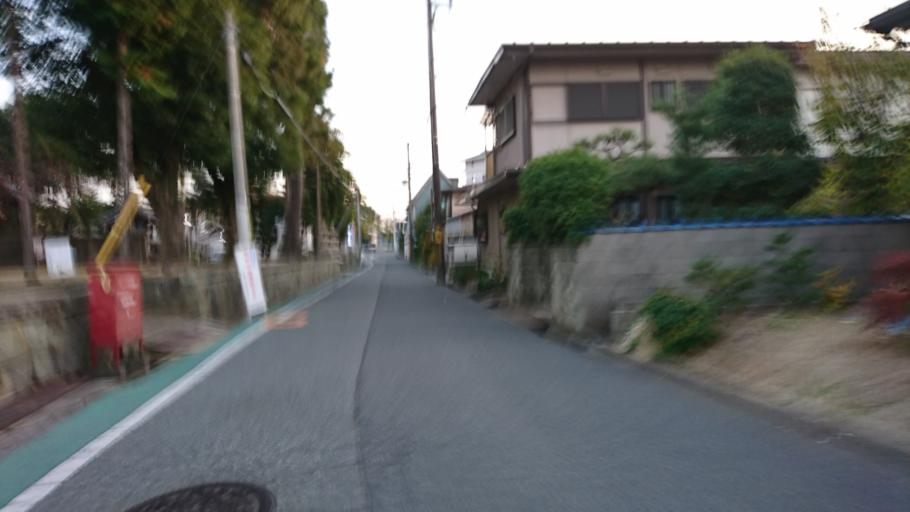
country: JP
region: Hyogo
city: Kakogawacho-honmachi
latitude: 34.7394
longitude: 134.8726
